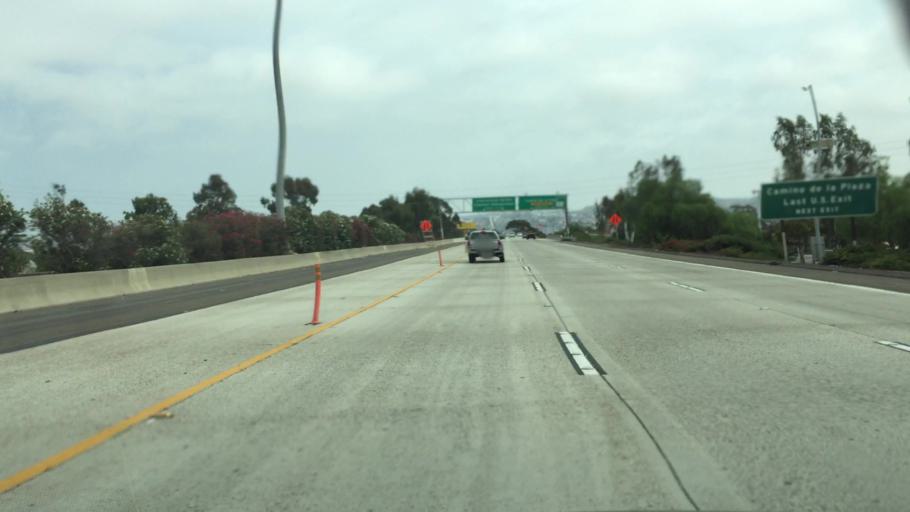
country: MX
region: Baja California
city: Tijuana
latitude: 32.5538
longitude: -117.0417
